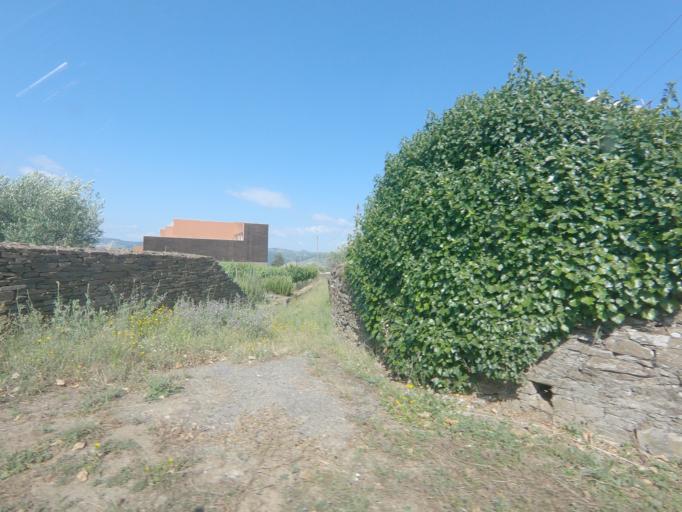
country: PT
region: Vila Real
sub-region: Sabrosa
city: Sabrosa
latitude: 41.2398
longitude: -7.5694
